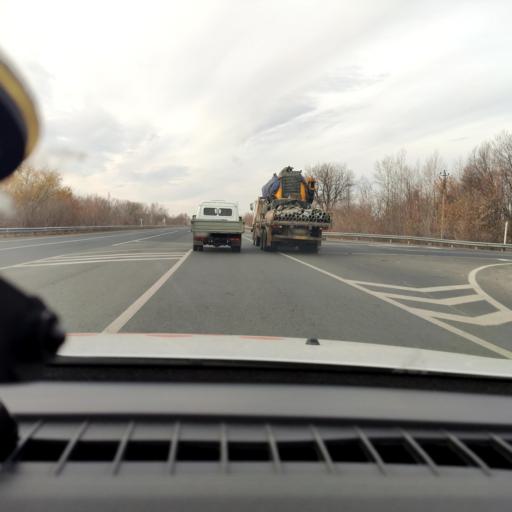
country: RU
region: Samara
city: Novokuybyshevsk
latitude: 53.1380
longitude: 49.9756
